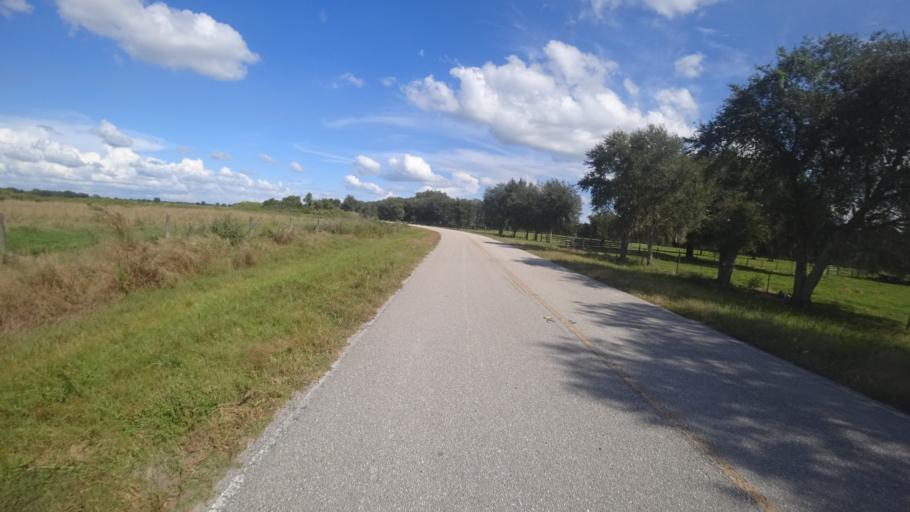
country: US
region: Florida
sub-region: DeSoto County
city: Arcadia
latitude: 27.2732
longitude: -82.0627
